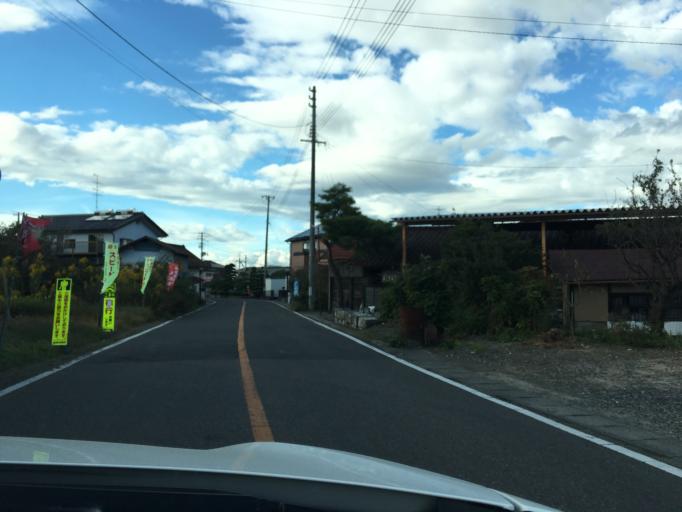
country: JP
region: Fukushima
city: Sukagawa
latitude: 37.2690
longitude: 140.4116
